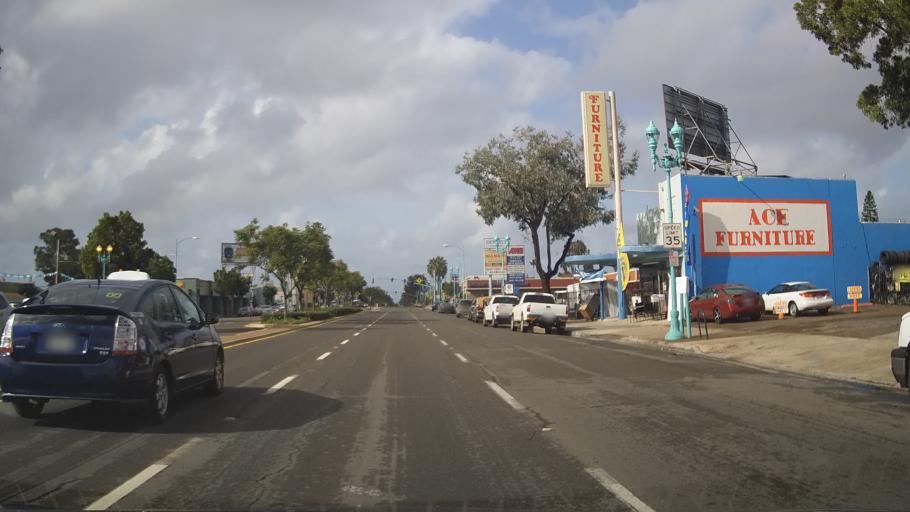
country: US
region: California
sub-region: San Diego County
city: San Diego
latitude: 32.7553
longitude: -117.1138
